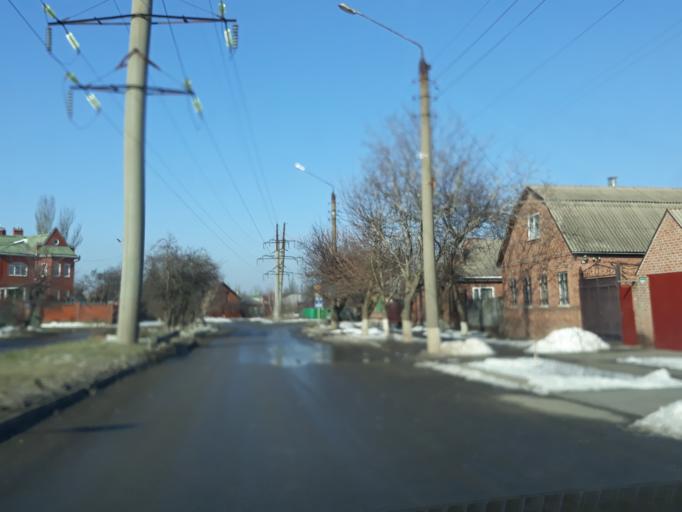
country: RU
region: Rostov
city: Taganrog
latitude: 47.2203
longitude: 38.8770
